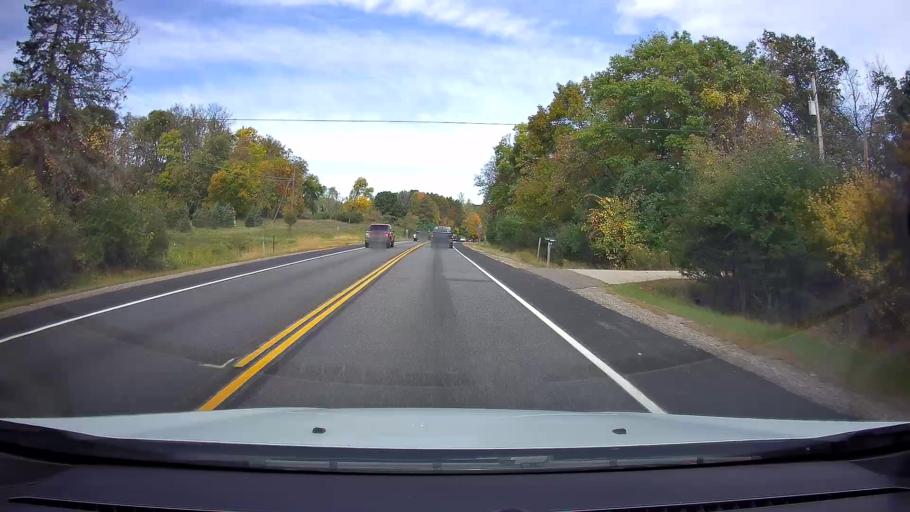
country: US
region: Minnesota
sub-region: Washington County
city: Scandia
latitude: 45.1851
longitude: -92.7709
